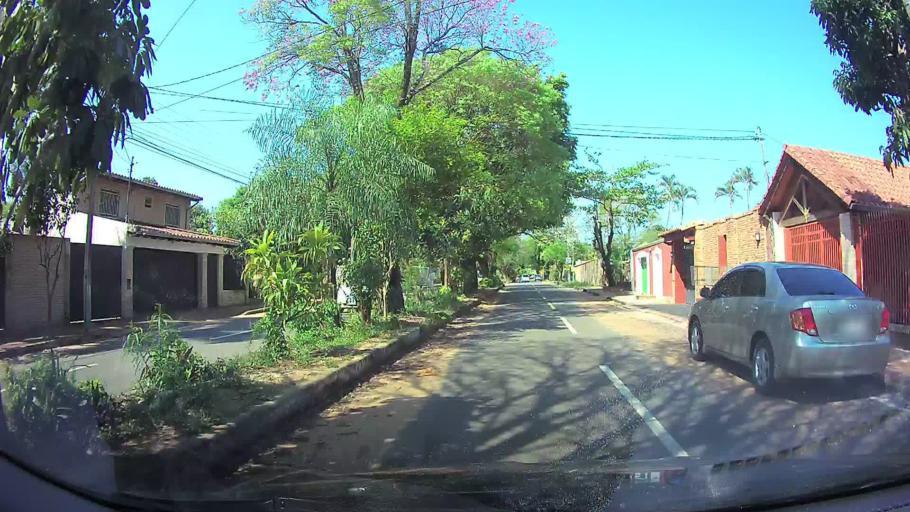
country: PY
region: Central
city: Limpio
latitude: -25.2362
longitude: -57.4771
